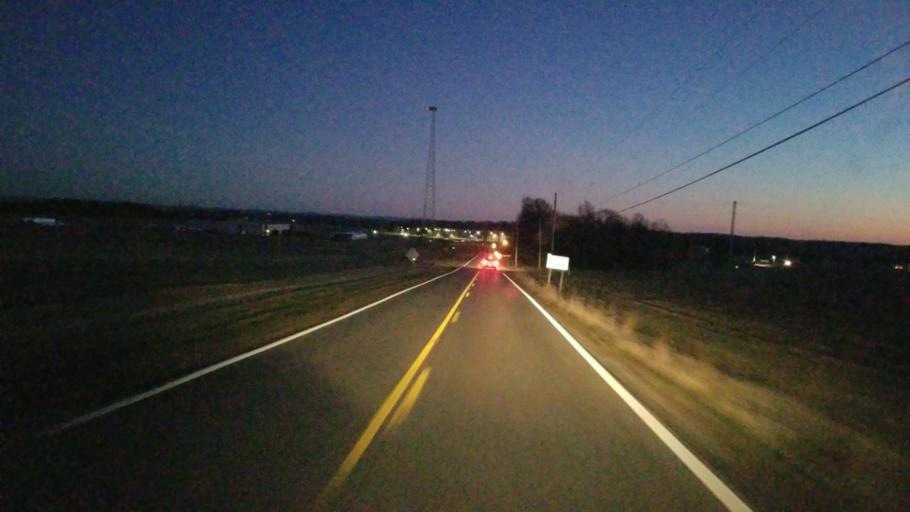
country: US
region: Ohio
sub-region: Highland County
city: Leesburg
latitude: 39.3361
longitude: -83.5503
